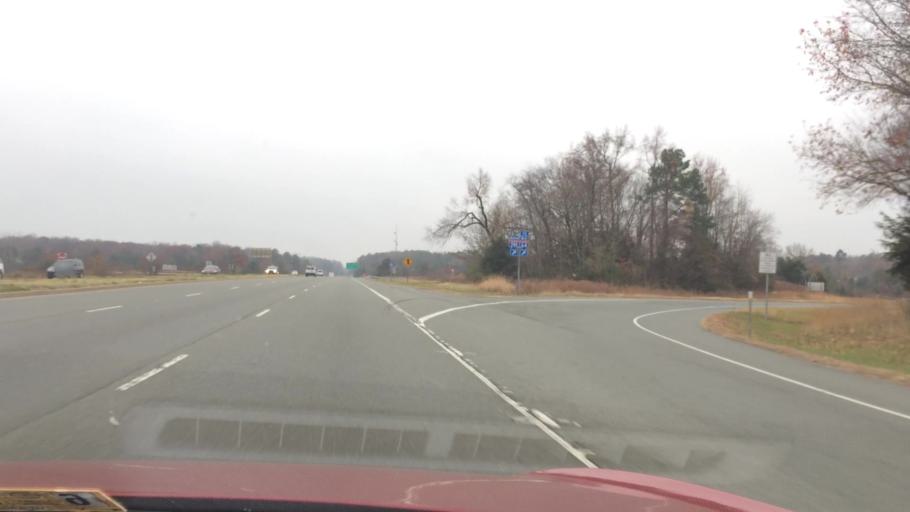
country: US
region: Virginia
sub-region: Henrico County
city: Glen Allen
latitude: 37.6623
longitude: -77.4603
